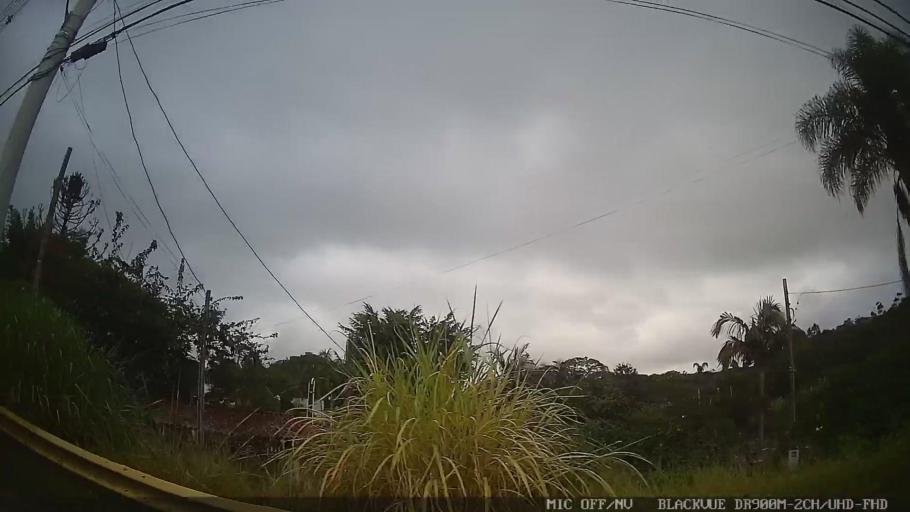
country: BR
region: Sao Paulo
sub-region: Biritiba-Mirim
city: Biritiba Mirim
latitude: -23.5475
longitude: -46.0863
